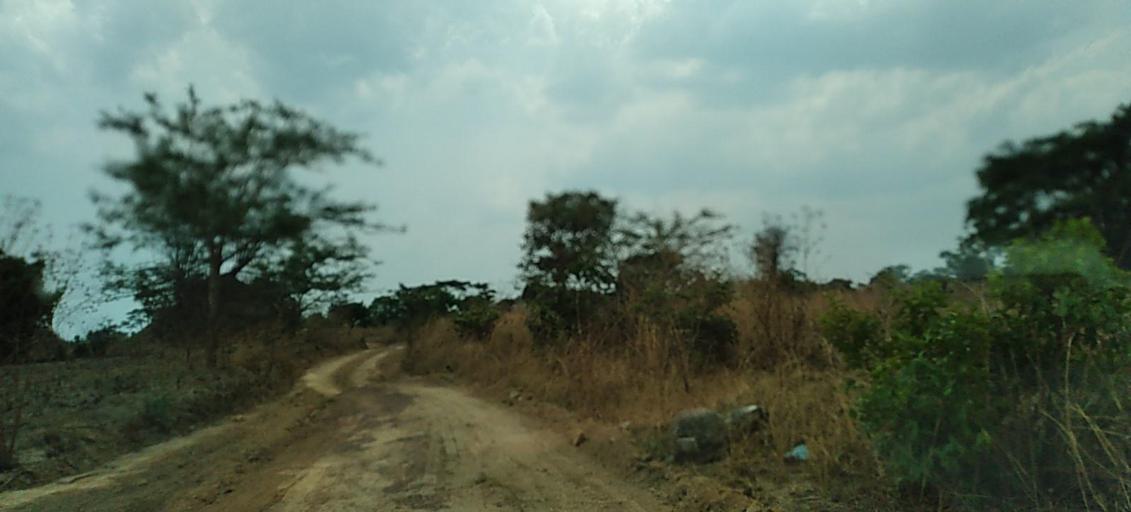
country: ZM
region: Copperbelt
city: Chililabombwe
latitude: -12.3517
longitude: 27.7979
